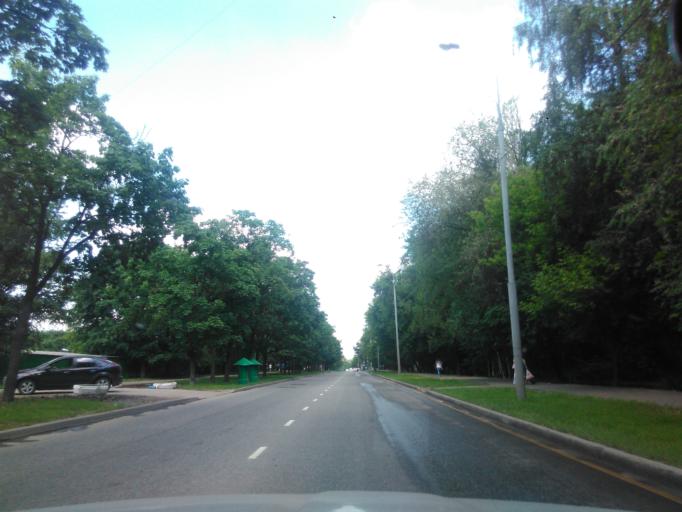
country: RU
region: Moscow
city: Zapadnoye Degunino
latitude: 55.8775
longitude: 37.5335
